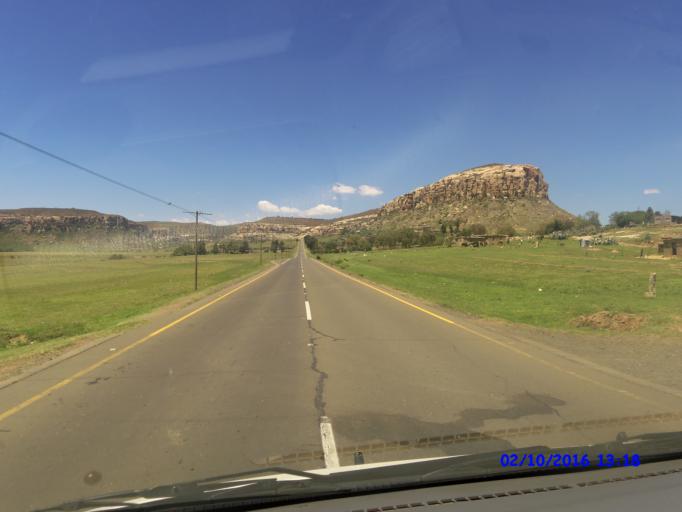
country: LS
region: Maseru
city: Nako
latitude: -29.4236
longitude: 27.6787
